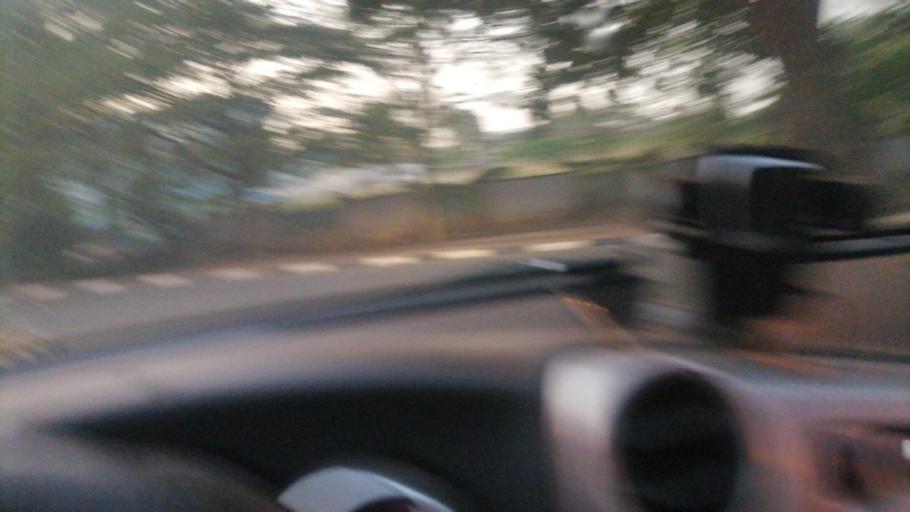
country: NG
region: Abuja Federal Capital Territory
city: Abuja
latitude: 9.0396
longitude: 7.4913
